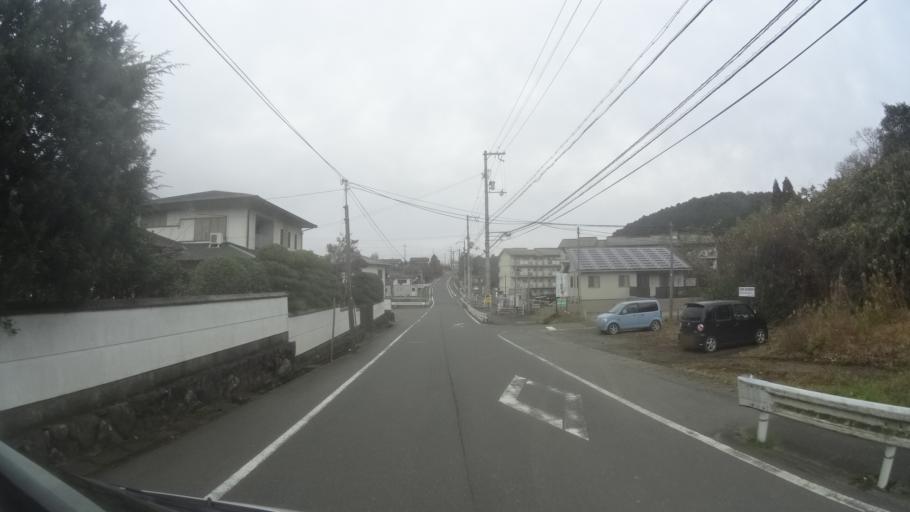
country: JP
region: Kyoto
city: Ayabe
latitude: 35.2910
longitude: 135.2611
